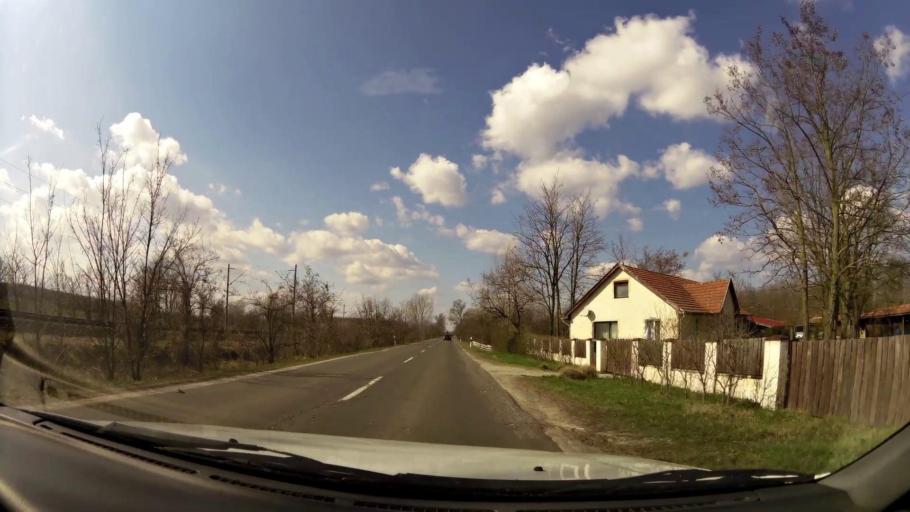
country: HU
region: Pest
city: Nagykata
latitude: 47.3921
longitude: 19.7681
